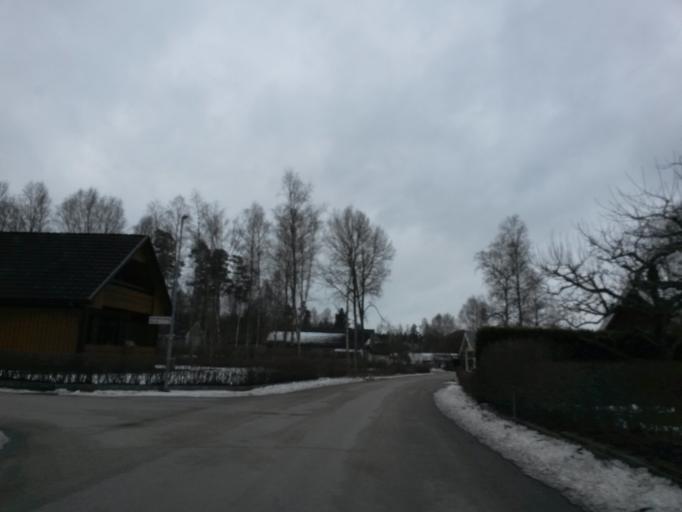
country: SE
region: Vaestra Goetaland
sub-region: Herrljunga Kommun
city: Herrljunga
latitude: 58.0787
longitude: 13.0434
